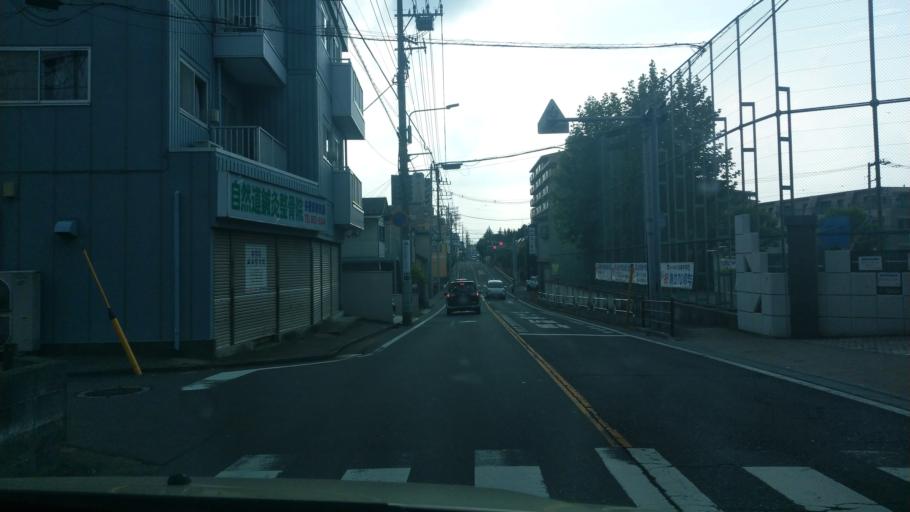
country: JP
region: Saitama
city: Yono
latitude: 35.8785
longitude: 139.6611
